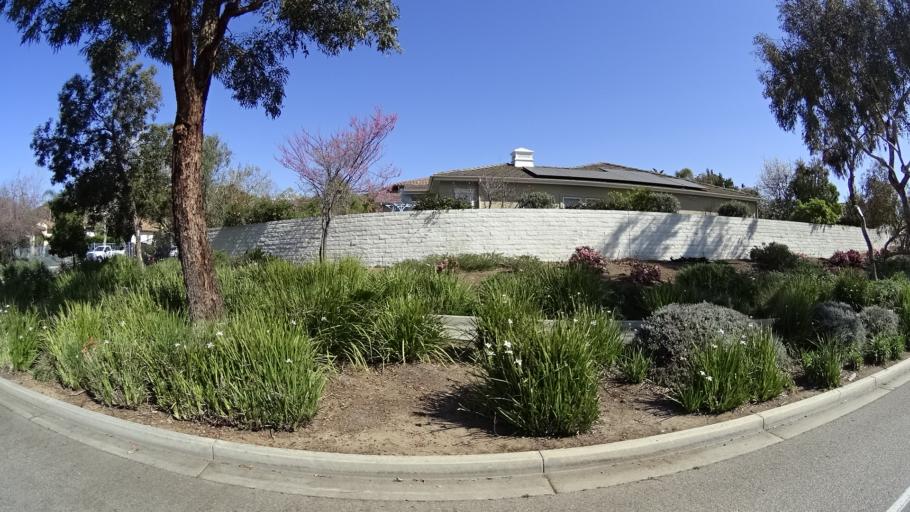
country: US
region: California
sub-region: Ventura County
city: Casa Conejo
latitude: 34.1564
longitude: -118.9765
